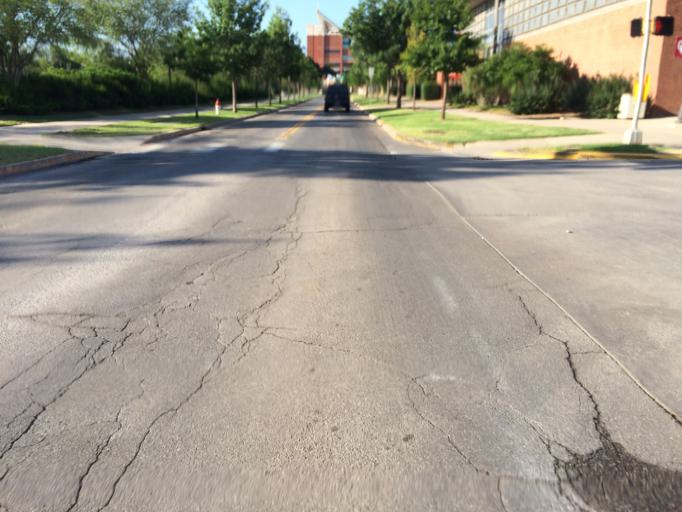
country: US
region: Oklahoma
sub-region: Cleveland County
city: Norman
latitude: 35.2099
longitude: -97.4413
